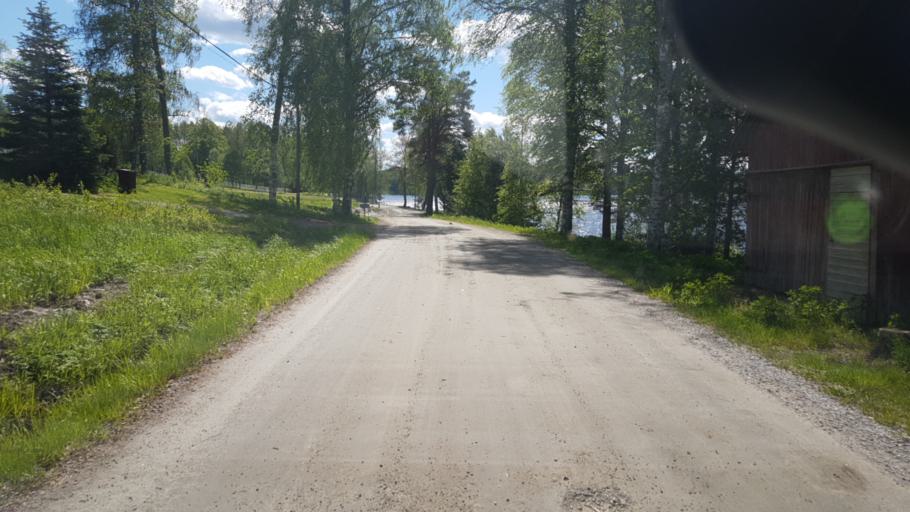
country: SE
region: Vaermland
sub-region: Arvika Kommun
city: Arvika
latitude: 59.7419
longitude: 12.8300
